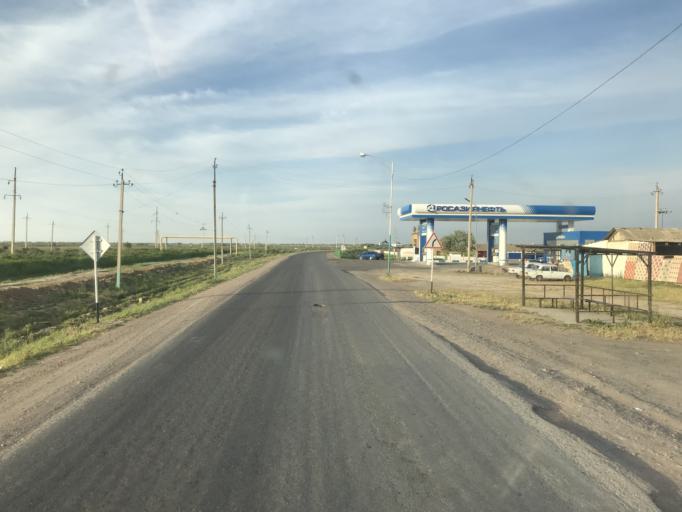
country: KZ
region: Ongtustik Qazaqstan
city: Asykata
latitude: 40.9057
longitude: 68.3659
